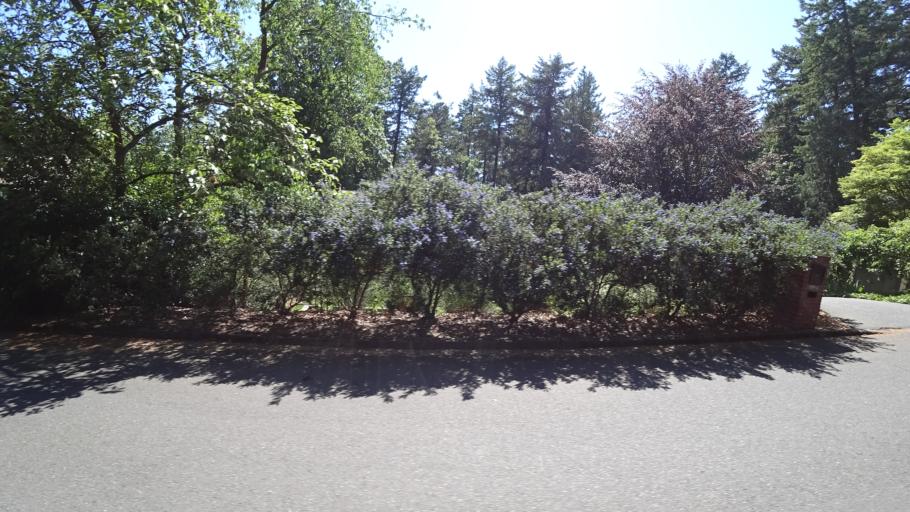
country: US
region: Oregon
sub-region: Washington County
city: West Slope
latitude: 45.4963
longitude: -122.7225
